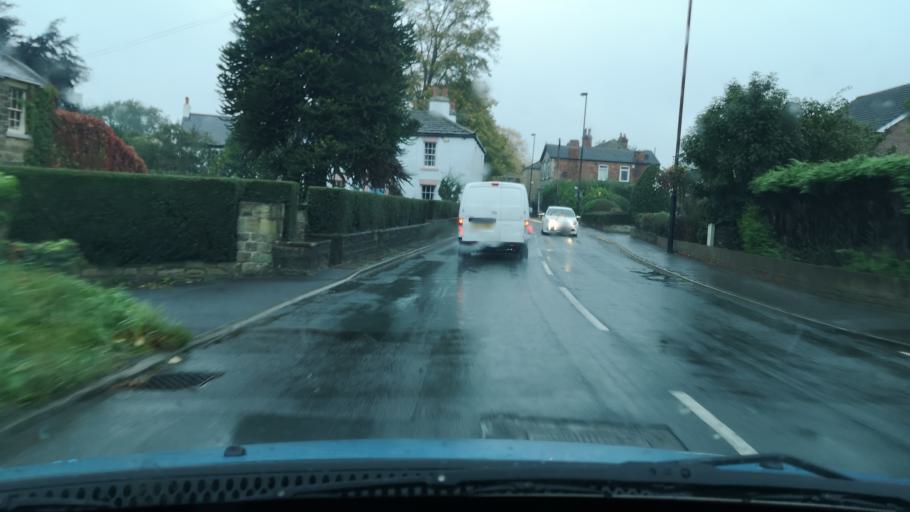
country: GB
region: England
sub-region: City and Borough of Wakefield
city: Low Ackworth
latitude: 53.6530
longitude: -1.3348
